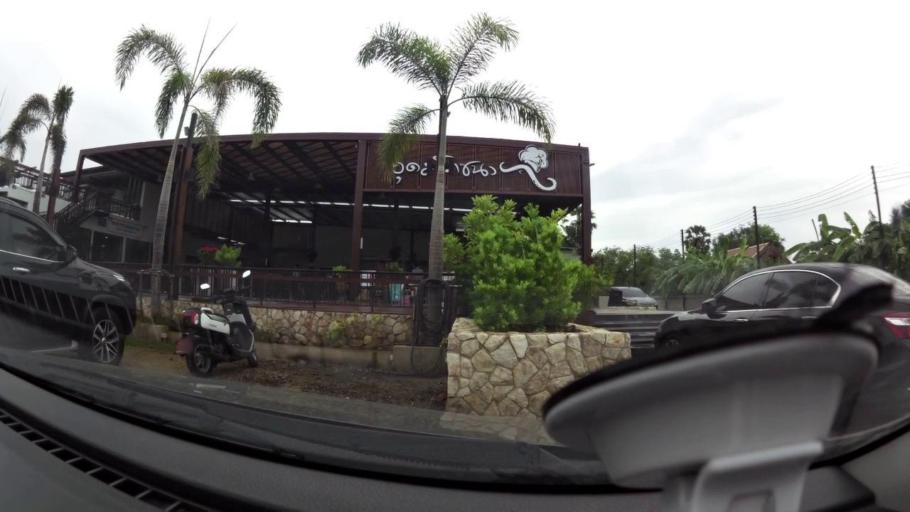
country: TH
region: Prachuap Khiri Khan
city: Pran Buri
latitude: 12.3683
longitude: 99.9997
